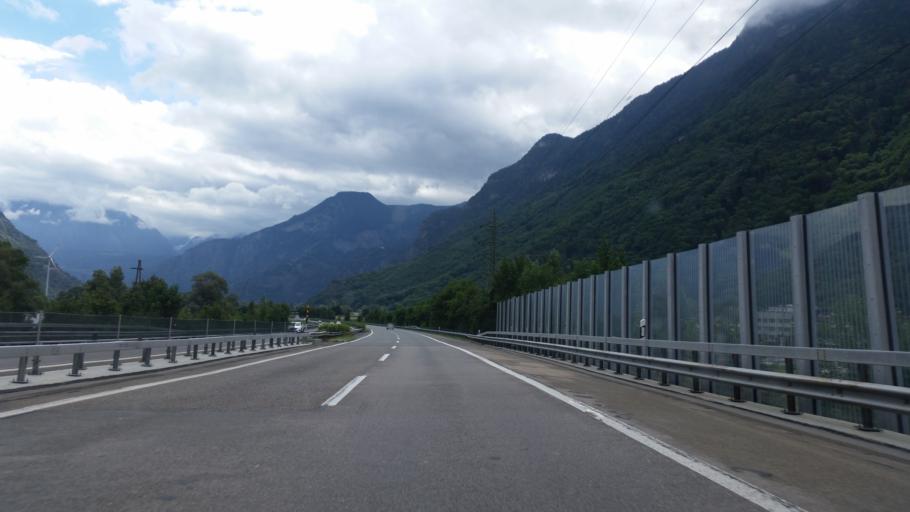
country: CH
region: Valais
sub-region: Martigny District
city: Evionnaz
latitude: 46.1753
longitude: 7.0260
